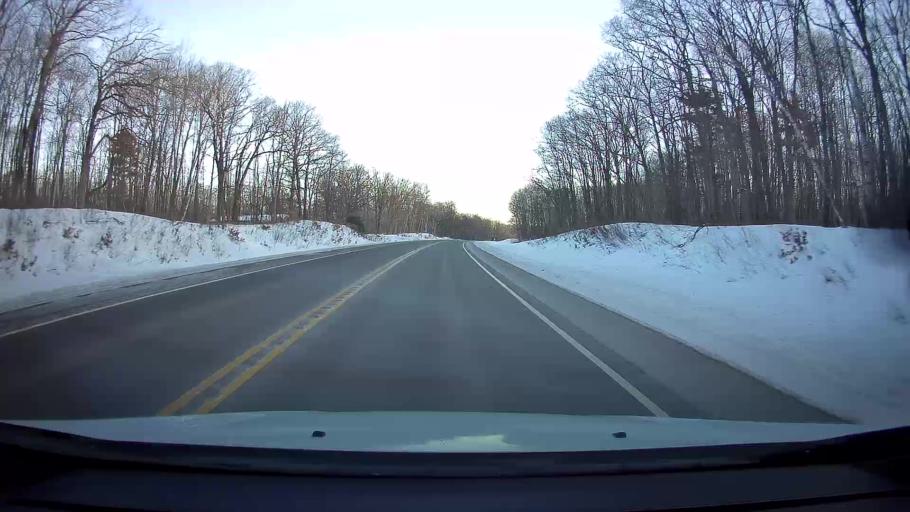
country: US
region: Wisconsin
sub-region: Washburn County
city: Shell Lake
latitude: 45.6722
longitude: -91.9932
